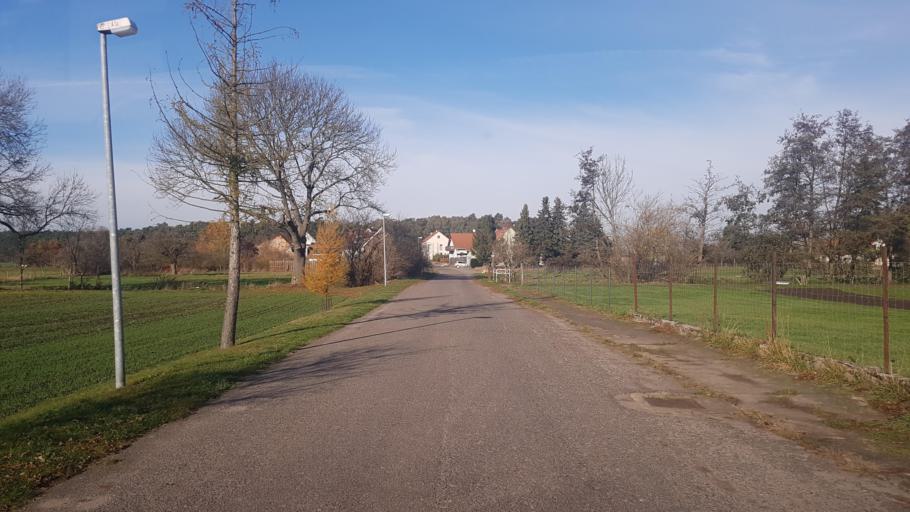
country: DE
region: Brandenburg
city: Niemegk
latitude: 52.1220
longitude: 12.6880
